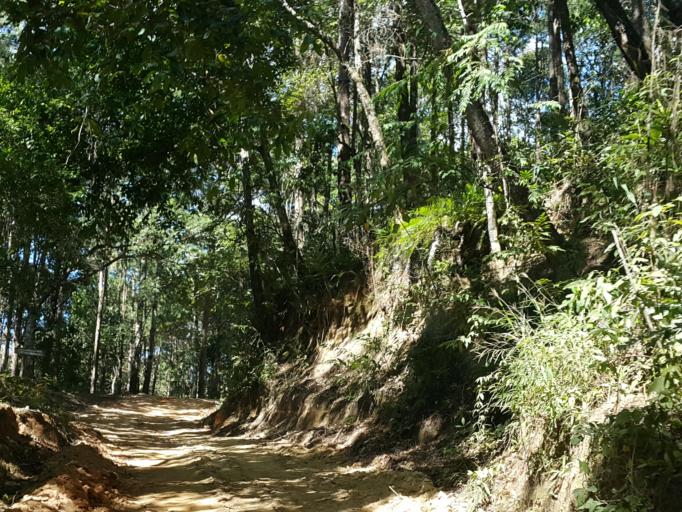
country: TH
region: Chiang Mai
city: Wiang Haeng
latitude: 19.5217
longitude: 98.8119
